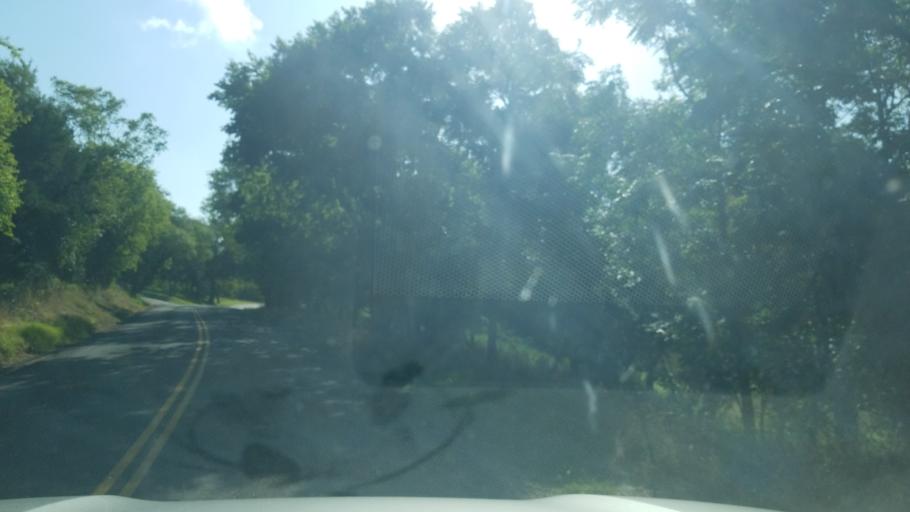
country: US
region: Texas
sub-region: Comal County
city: Bulverde
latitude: 29.7328
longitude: -98.4544
